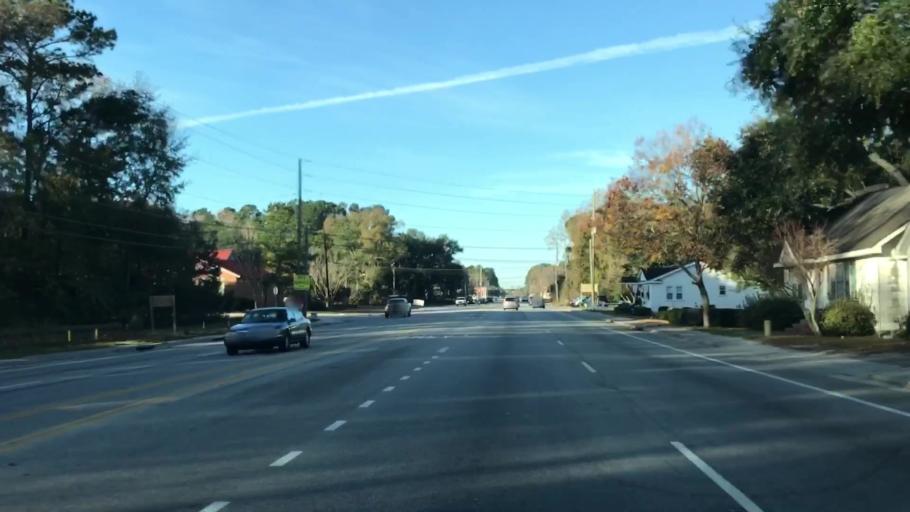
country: US
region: South Carolina
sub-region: Berkeley County
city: Ladson
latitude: 32.9867
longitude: -80.1052
